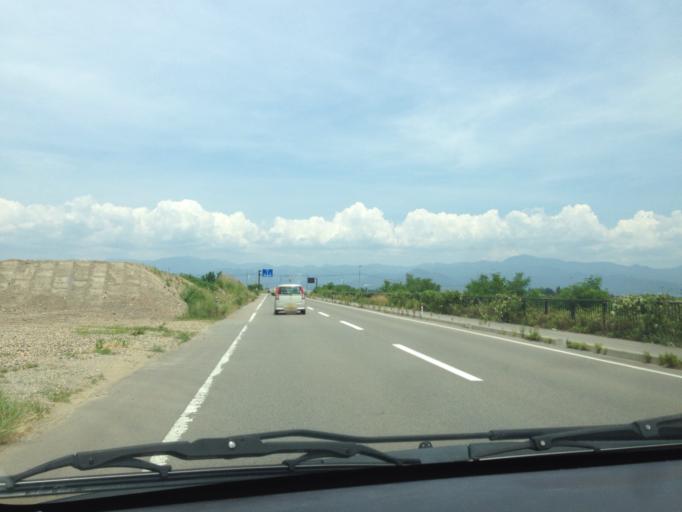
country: JP
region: Fukushima
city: Kitakata
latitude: 37.6091
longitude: 139.8496
